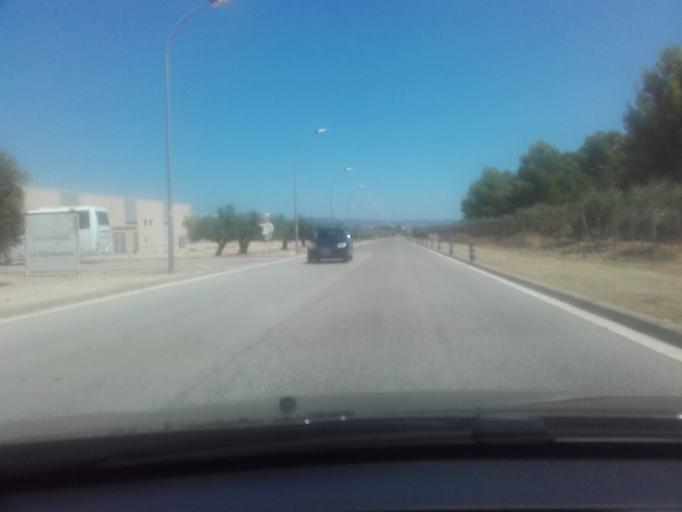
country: ES
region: Catalonia
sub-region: Provincia de Tarragona
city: Santa Oliva
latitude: 41.2691
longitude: 1.5187
